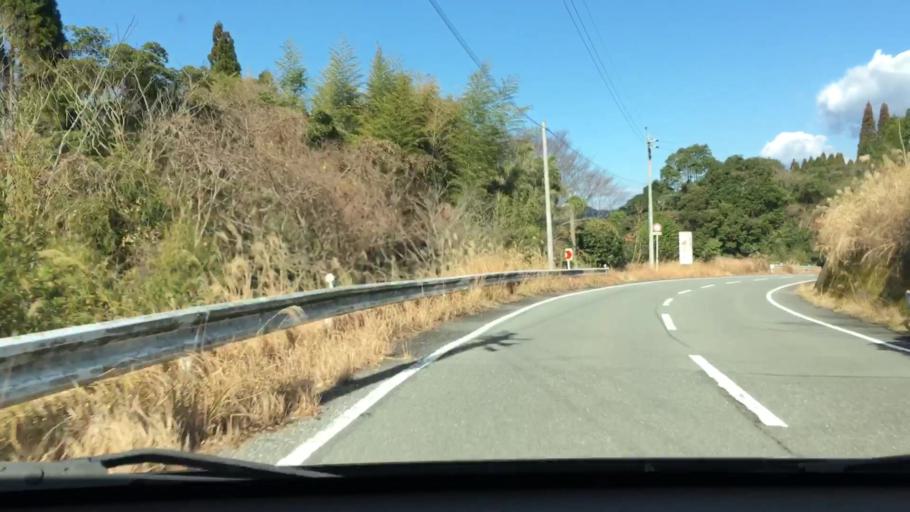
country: JP
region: Kagoshima
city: Ijuin
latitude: 31.7208
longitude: 130.4159
